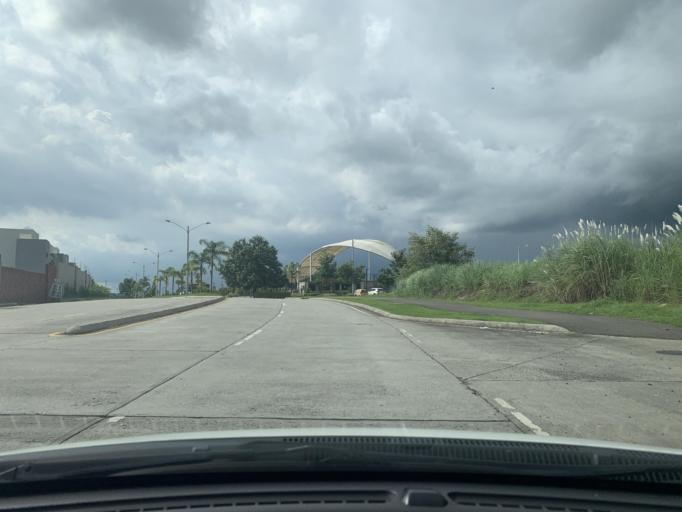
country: PA
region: Panama
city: San Miguelito
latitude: 9.0909
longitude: -79.4682
